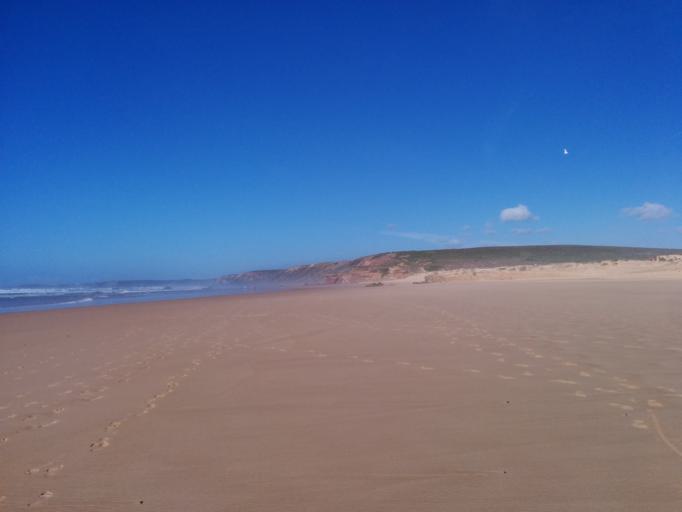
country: PT
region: Faro
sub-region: Vila do Bispo
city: Vila do Bispo
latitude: 37.2014
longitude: -8.9006
